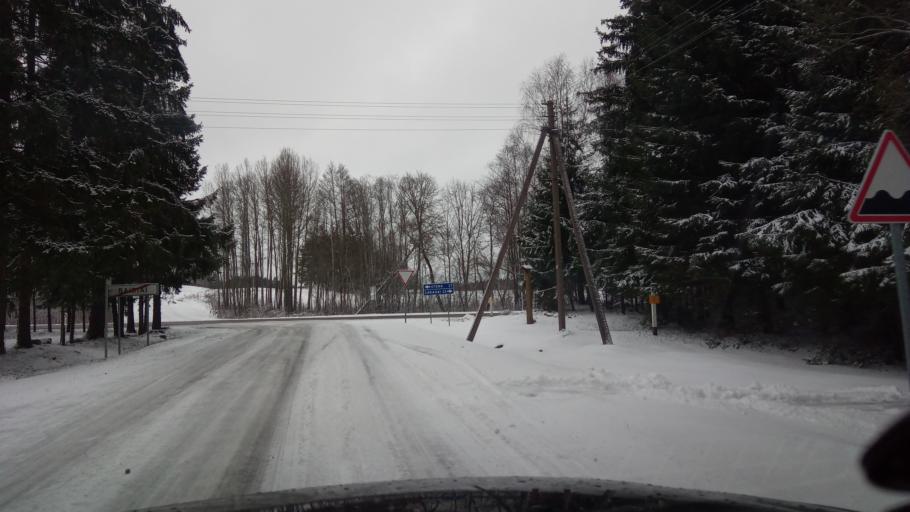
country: LT
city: Zarasai
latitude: 55.6298
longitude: 25.9549
